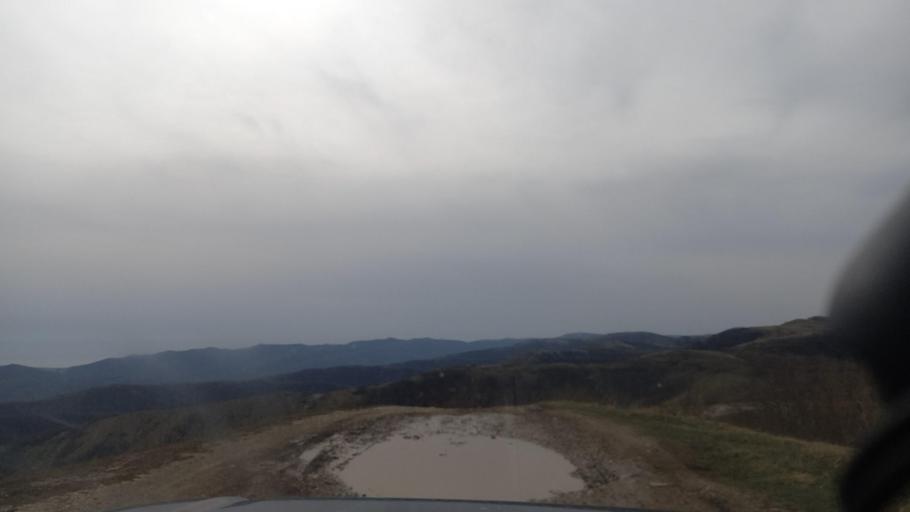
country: RU
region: Krasnodarskiy
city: Divnomorskoye
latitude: 44.6105
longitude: 38.2363
